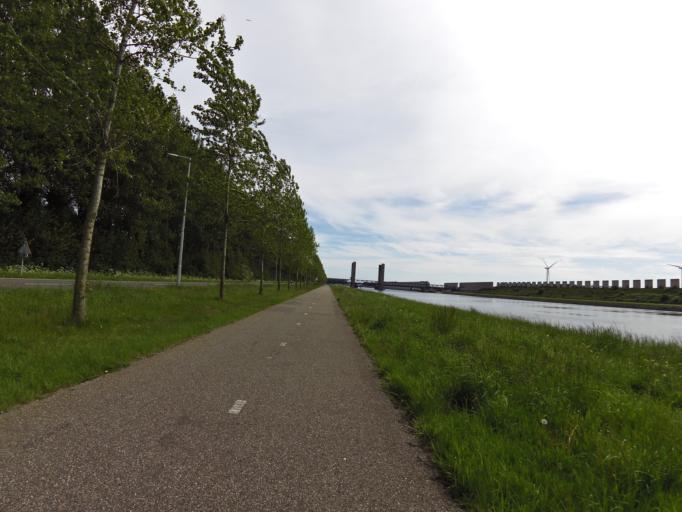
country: NL
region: South Holland
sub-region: Gemeente Maassluis
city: Maassluis
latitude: 51.9089
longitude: 4.2267
